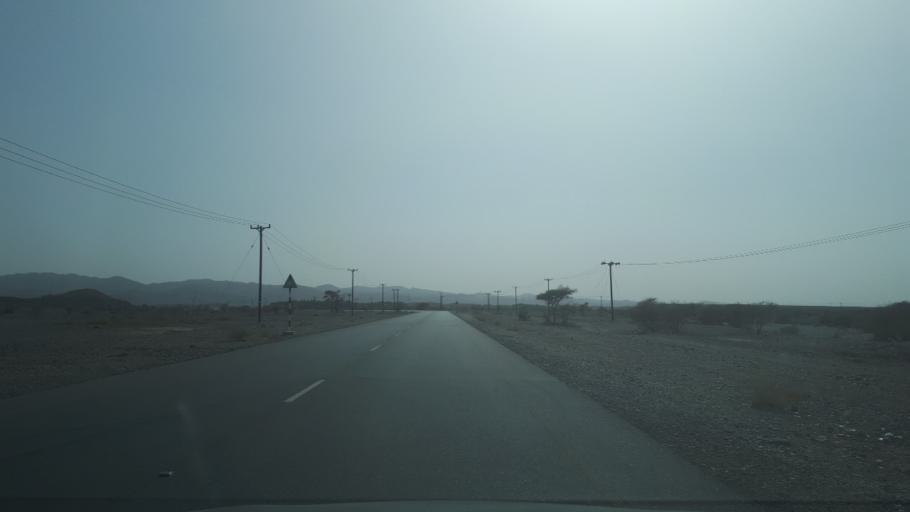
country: OM
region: Az Zahirah
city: `Ibri
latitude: 23.0935
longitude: 56.8382
